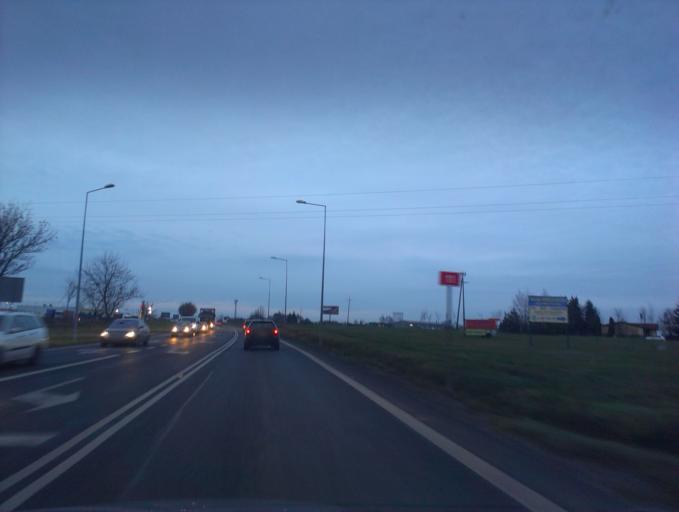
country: PL
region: Greater Poland Voivodeship
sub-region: Powiat poznanski
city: Zlotniki
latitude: 52.5603
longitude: 16.8354
